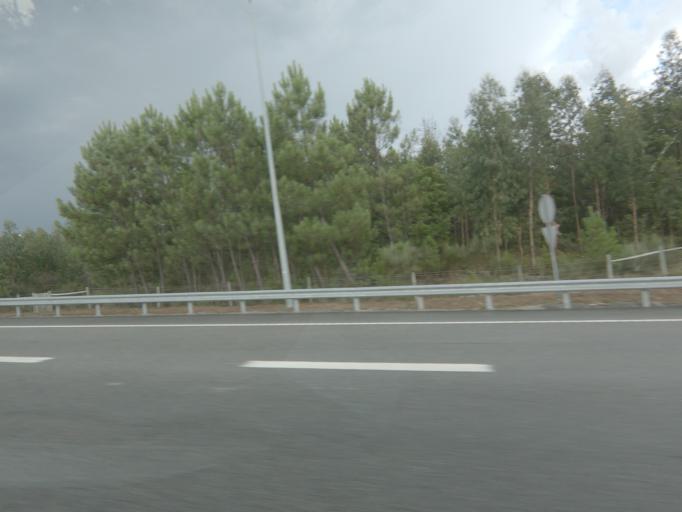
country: PT
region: Viseu
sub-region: Viseu
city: Abraveses
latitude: 40.6795
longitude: -7.9680
